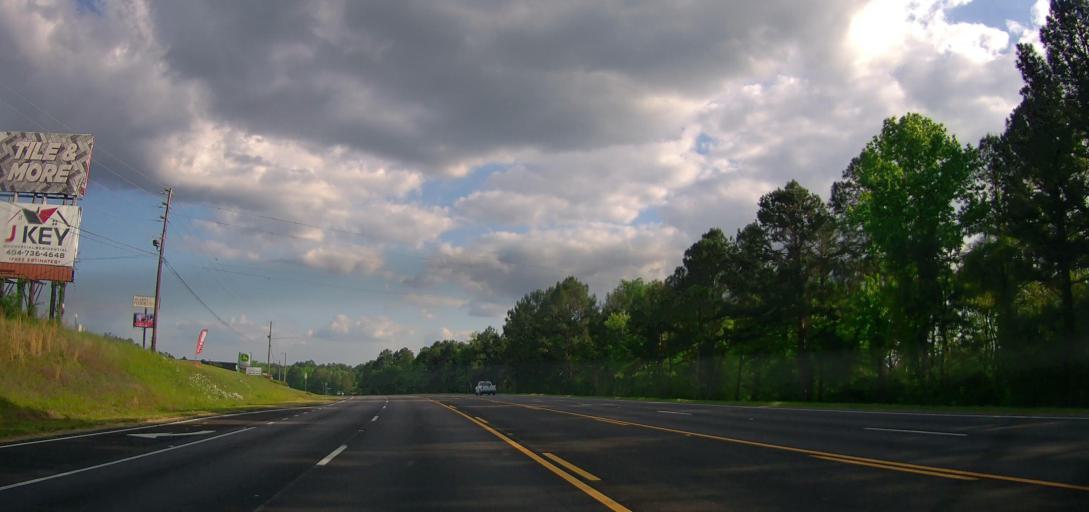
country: US
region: Georgia
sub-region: Baldwin County
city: Milledgeville
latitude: 33.1355
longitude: -83.2708
